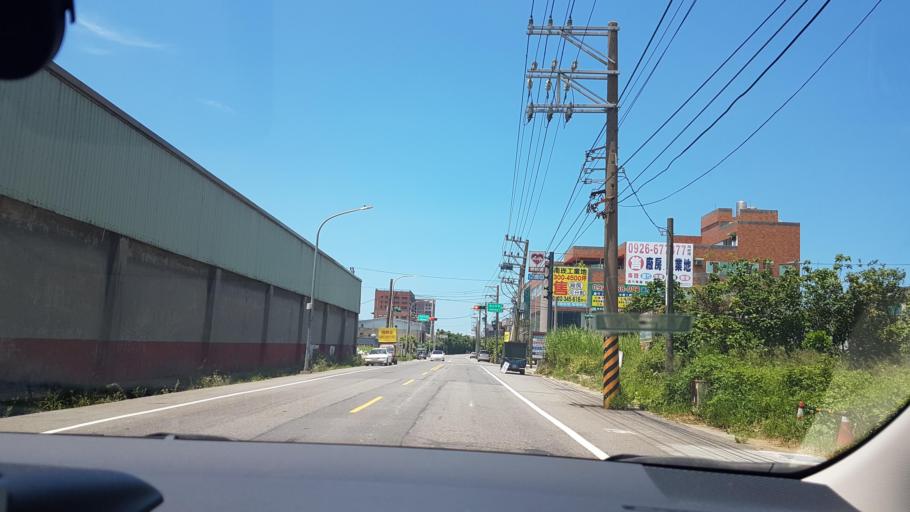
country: TW
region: Taiwan
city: Taoyuan City
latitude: 25.1049
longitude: 121.2584
